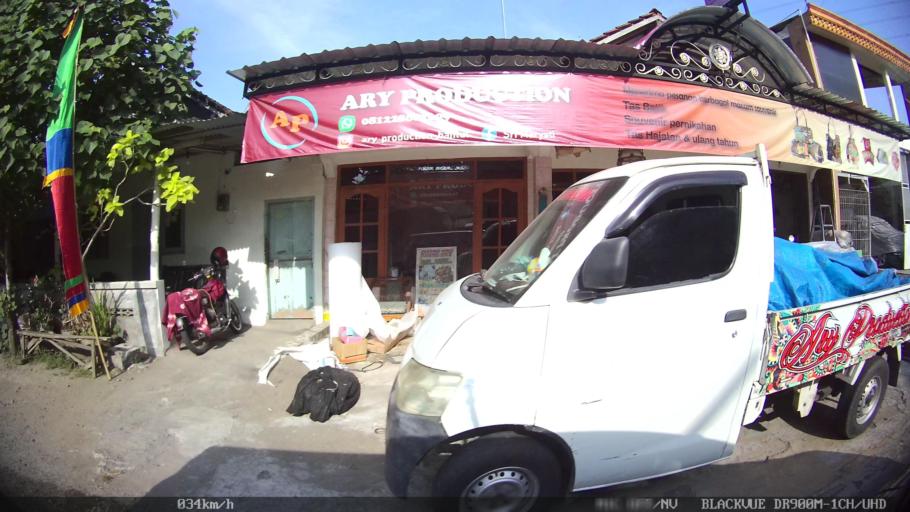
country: ID
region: Daerah Istimewa Yogyakarta
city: Bantul
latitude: -7.8741
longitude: 110.3152
